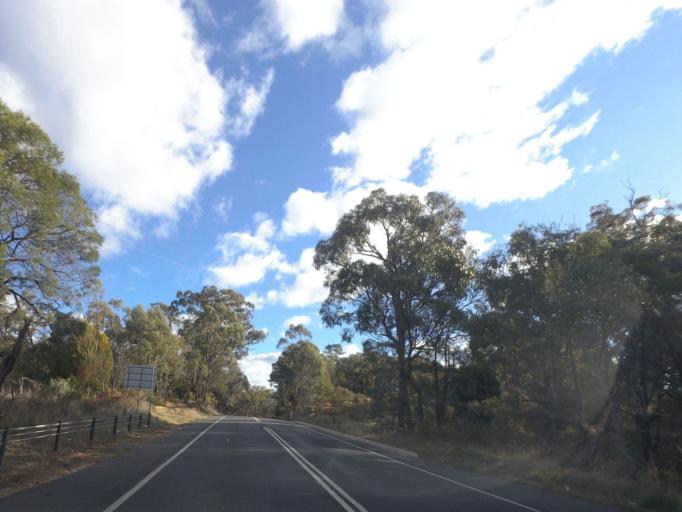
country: AU
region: Victoria
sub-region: Mount Alexander
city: Castlemaine
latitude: -37.1053
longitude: 144.3089
